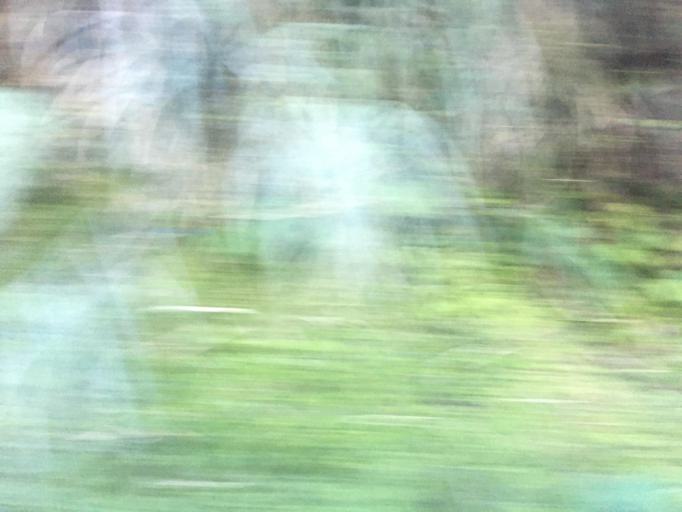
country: TW
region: Taiwan
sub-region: Yilan
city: Yilan
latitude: 24.5342
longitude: 121.5171
